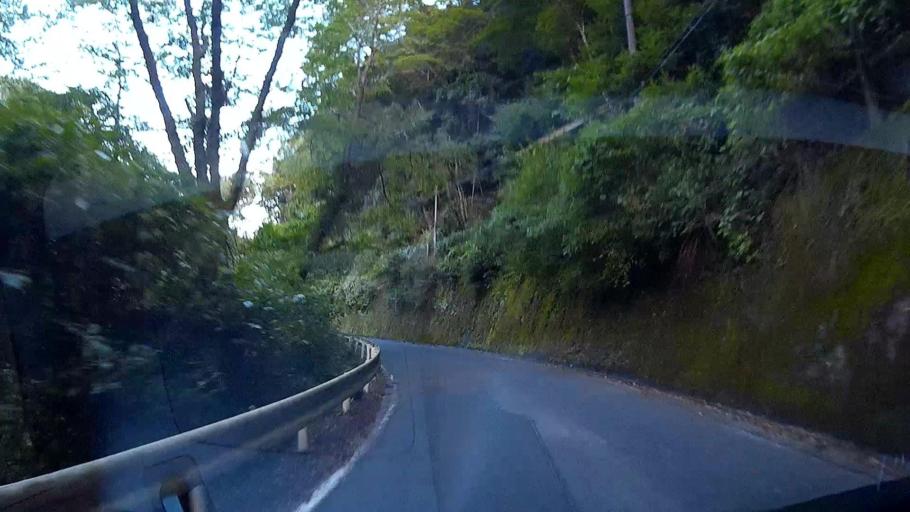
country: JP
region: Shizuoka
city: Shizuoka-shi
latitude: 35.1363
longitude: 138.2784
